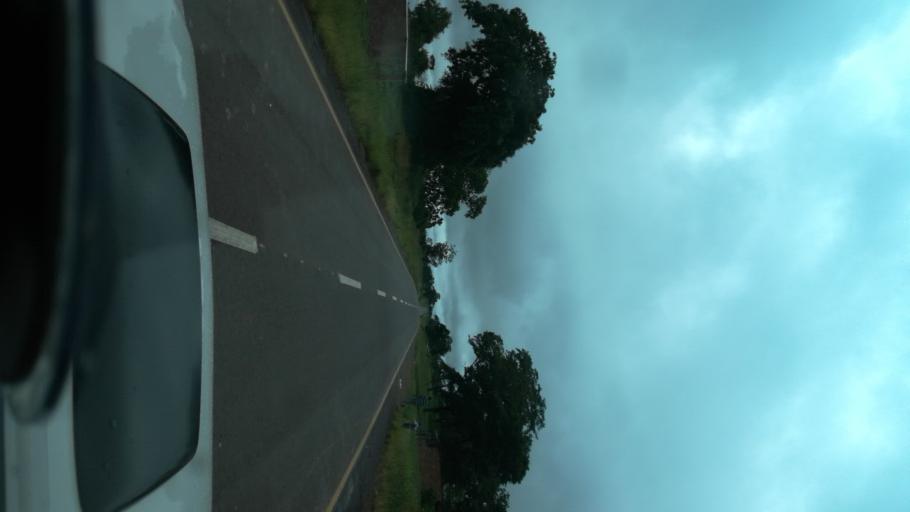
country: ZM
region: Luapula
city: Mansa
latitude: -10.9871
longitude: 28.1119
